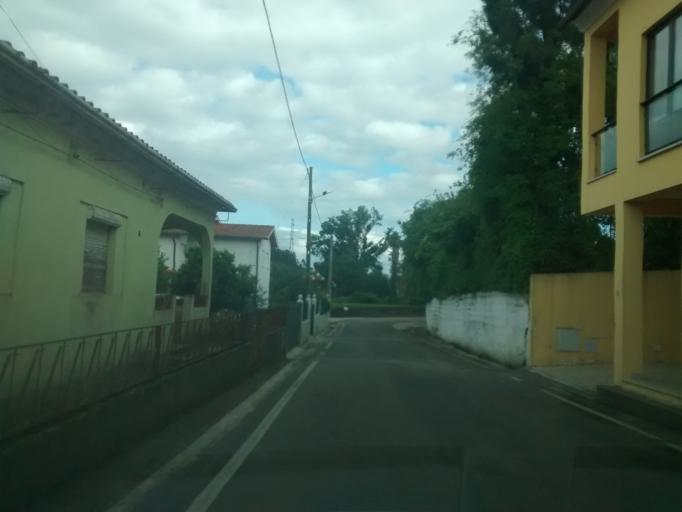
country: PT
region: Aveiro
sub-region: Anadia
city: Sangalhos
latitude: 40.4378
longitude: -8.4974
